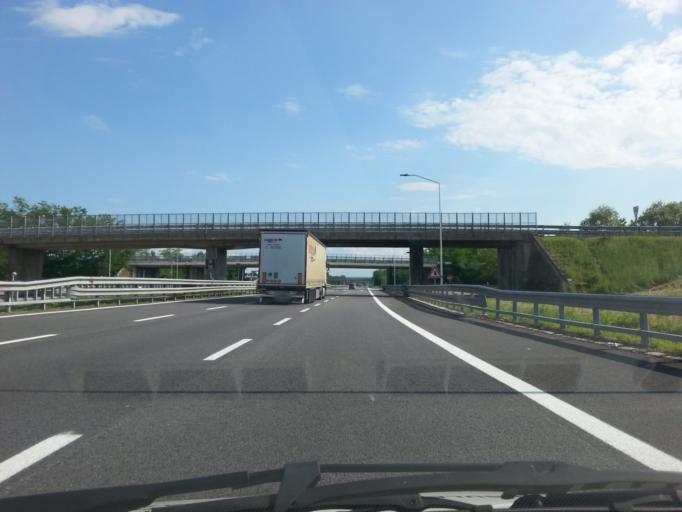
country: IT
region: Piedmont
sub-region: Provincia di Torino
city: Carmagnola
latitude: 44.8526
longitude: 7.7485
